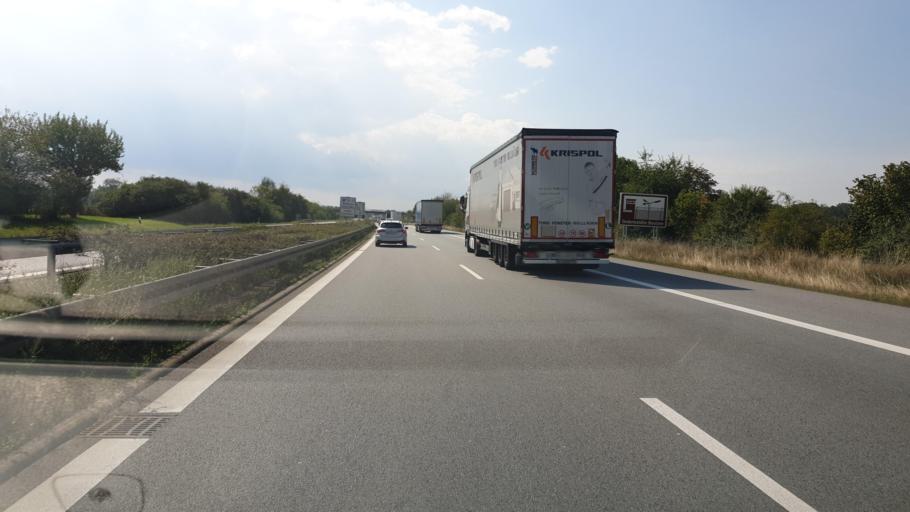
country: DE
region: Saxony
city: Kubschutz
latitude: 51.2030
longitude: 14.4850
